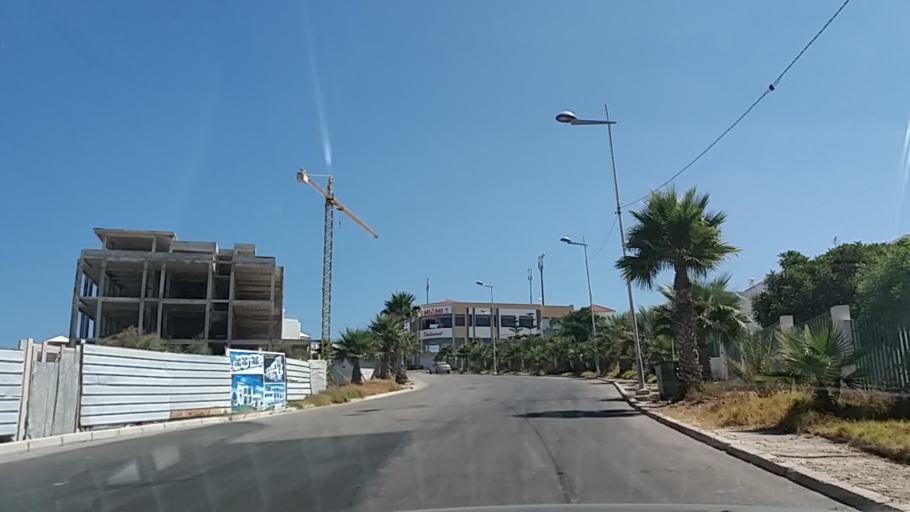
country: MA
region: Tanger-Tetouan
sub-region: Tanger-Assilah
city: Tangier
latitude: 35.7895
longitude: -5.7562
